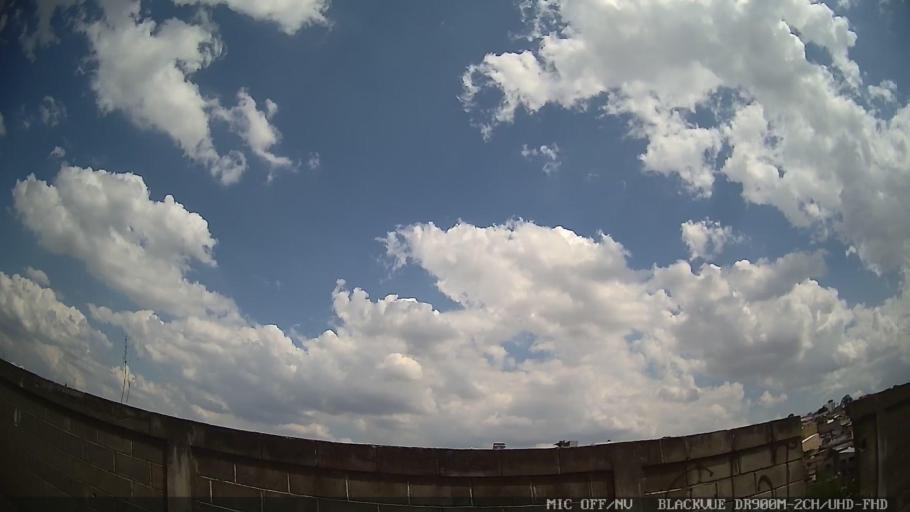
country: BR
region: Sao Paulo
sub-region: Ferraz De Vasconcelos
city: Ferraz de Vasconcelos
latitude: -23.5494
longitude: -46.4678
